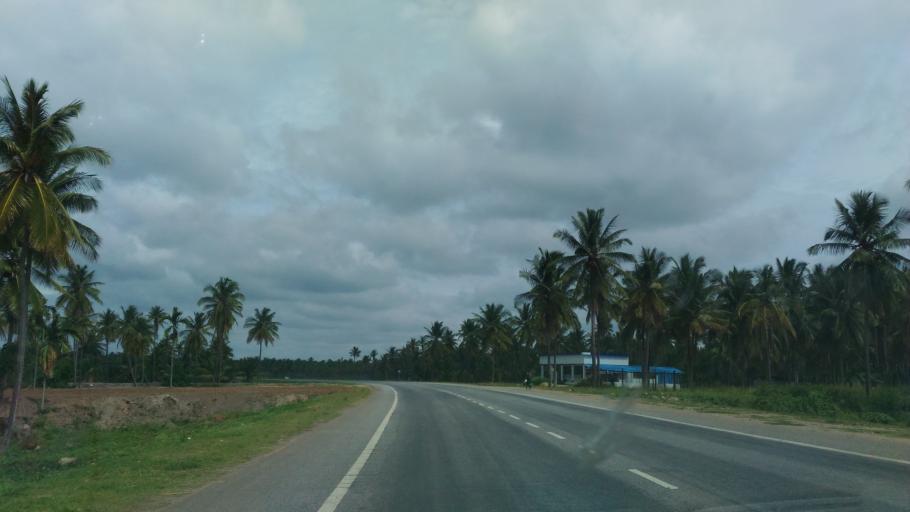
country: IN
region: Karnataka
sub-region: Hassan
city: Channarayapatna
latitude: 12.9319
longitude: 76.4043
